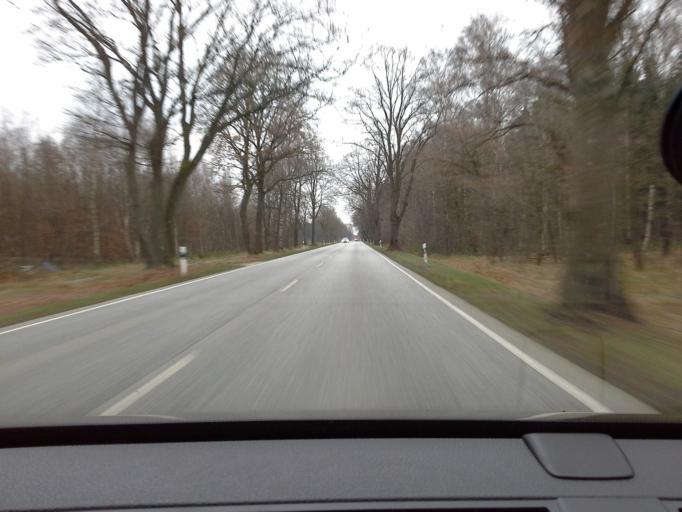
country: DE
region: Schleswig-Holstein
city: Langeln
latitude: 53.8159
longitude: 9.8809
